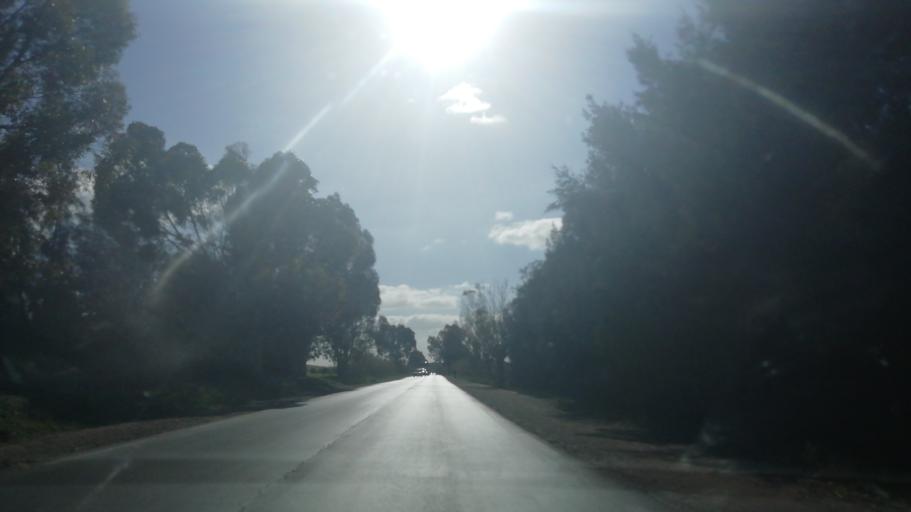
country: DZ
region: Mostaganem
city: Mostaganem
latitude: 35.9615
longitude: 0.2532
